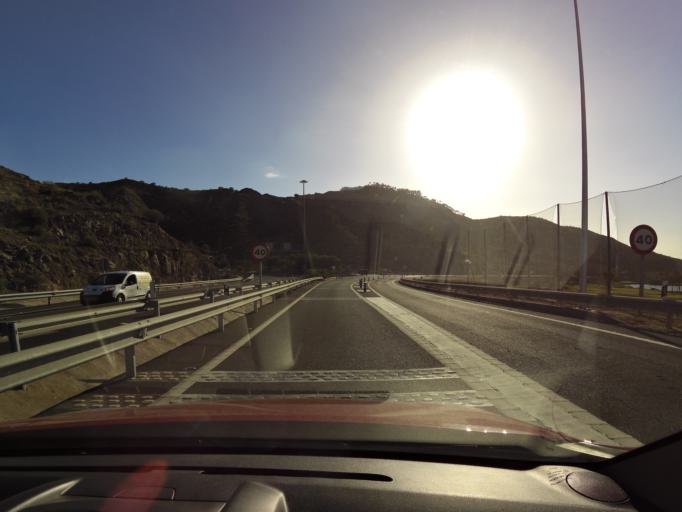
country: ES
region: Canary Islands
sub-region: Provincia de Las Palmas
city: Puerto Rico
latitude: 27.7996
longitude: -15.7082
